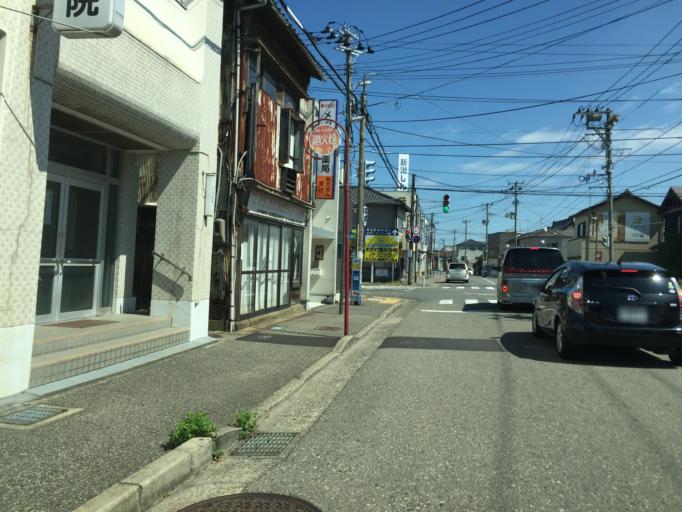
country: JP
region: Niigata
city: Niigata-shi
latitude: 37.9323
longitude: 139.0503
